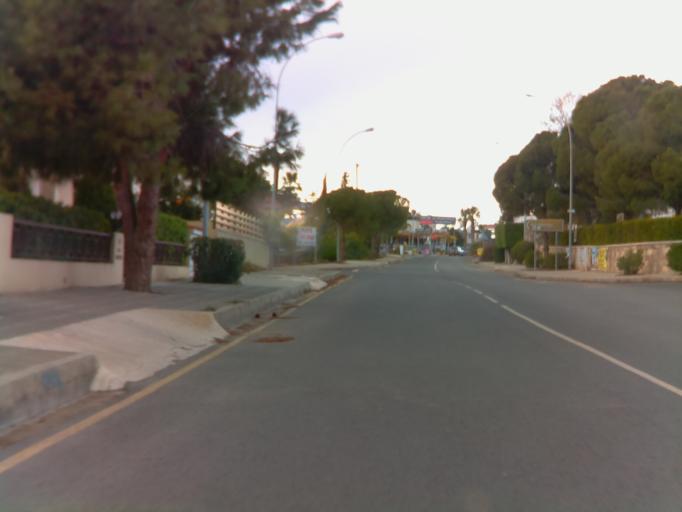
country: CY
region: Pafos
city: Pegeia
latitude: 34.8564
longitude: 32.3677
